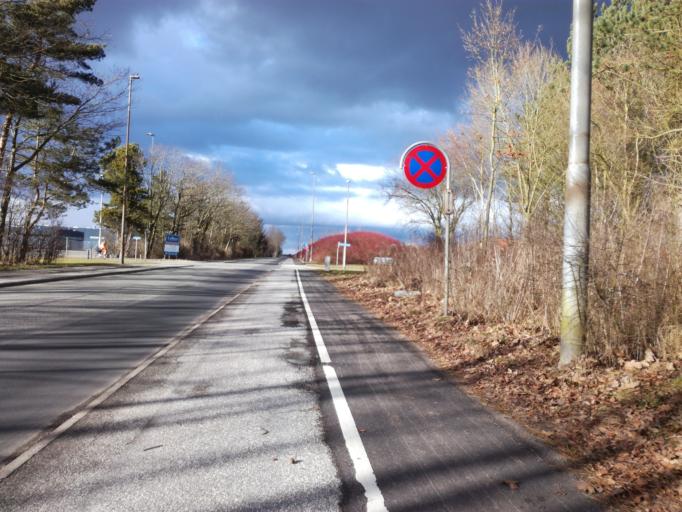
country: DK
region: South Denmark
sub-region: Fredericia Kommune
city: Fredericia
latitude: 55.5896
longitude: 9.7676
